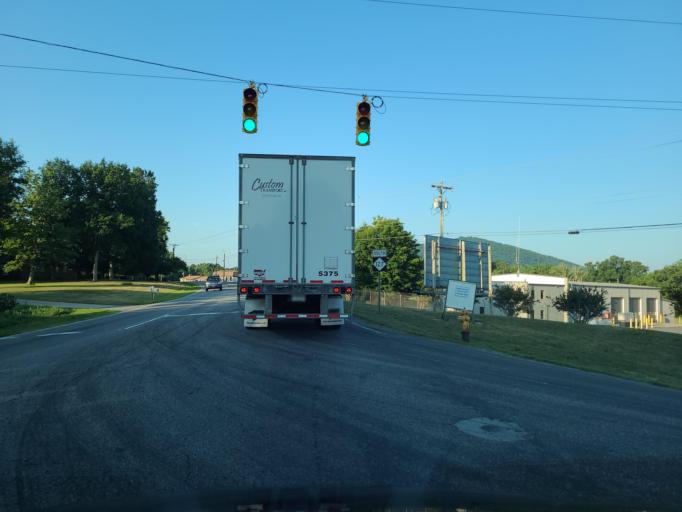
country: US
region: North Carolina
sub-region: Catawba County
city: Mountain View
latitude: 35.6762
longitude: -81.3851
